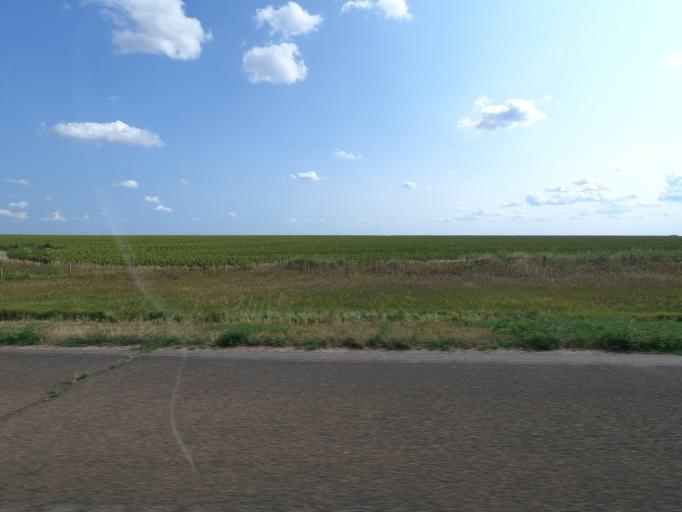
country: US
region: Kansas
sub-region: Logan County
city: Oakley
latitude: 39.1122
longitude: -100.7276
